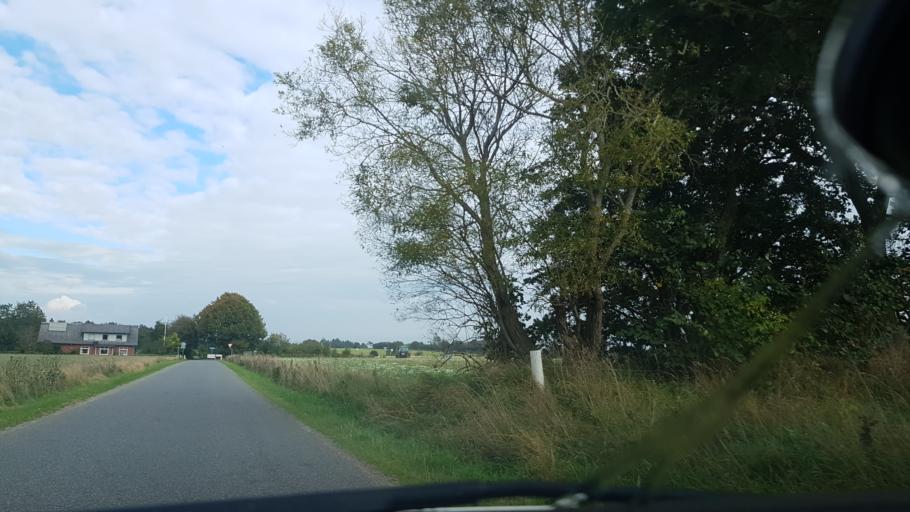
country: DK
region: South Denmark
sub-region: Vejen Kommune
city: Brorup
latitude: 55.4866
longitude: 8.9856
